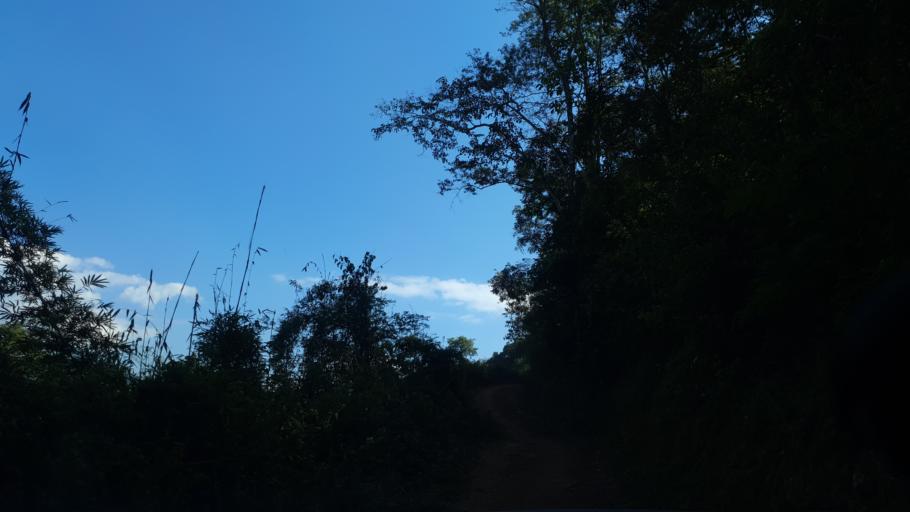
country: TH
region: Mae Hong Son
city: Mae Hi
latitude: 19.3021
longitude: 98.7003
